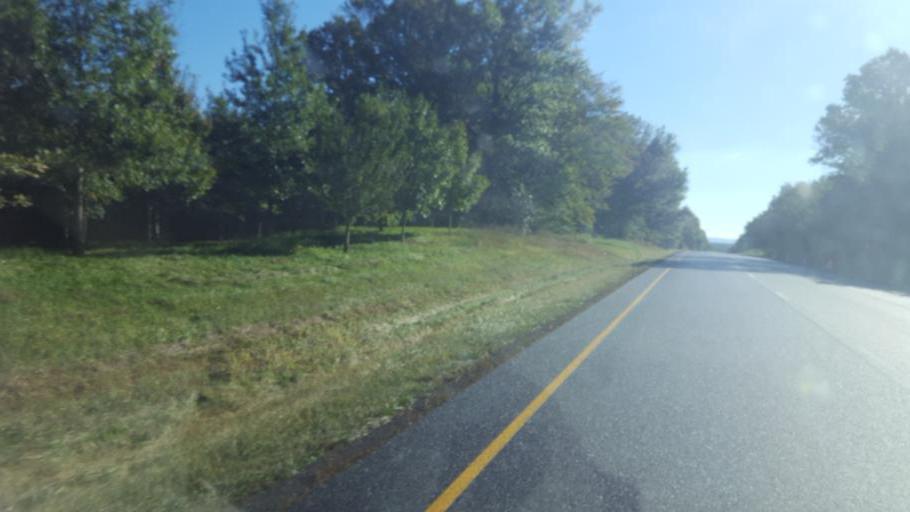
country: US
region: Maryland
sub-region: Washington County
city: Wilson-Conococheague
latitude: 39.6510
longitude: -77.8820
